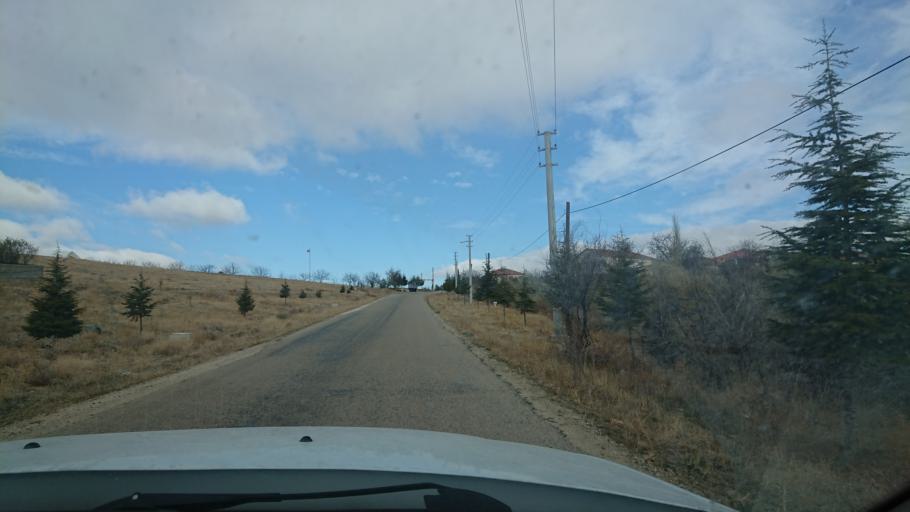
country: TR
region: Aksaray
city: Agacoren
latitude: 38.8250
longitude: 33.9578
